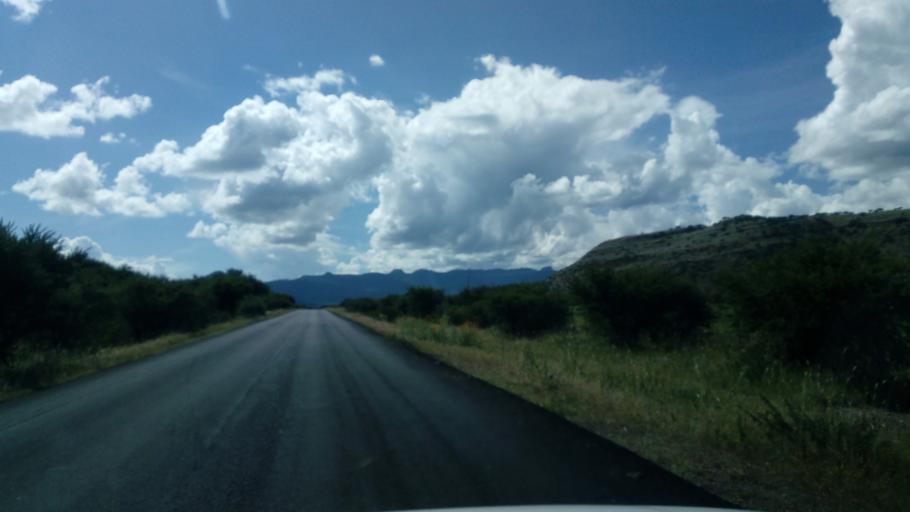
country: MX
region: Durango
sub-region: Durango
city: Jose Refugio Salcido
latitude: 23.8206
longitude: -104.4830
